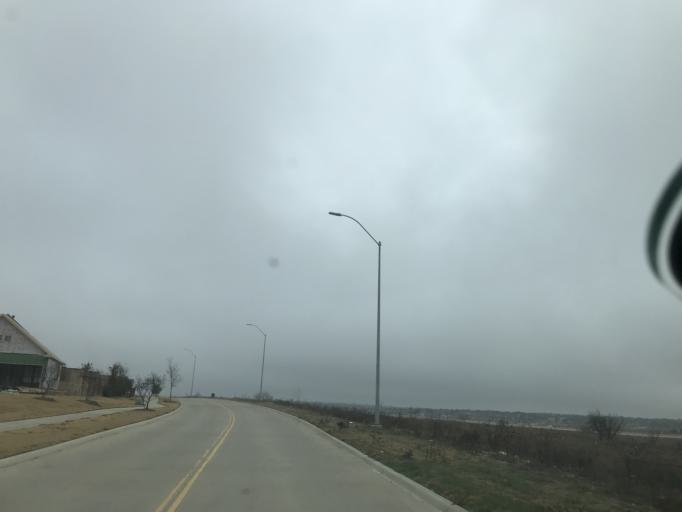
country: US
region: Texas
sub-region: Tarrant County
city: Crowley
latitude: 32.6107
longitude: -97.4174
